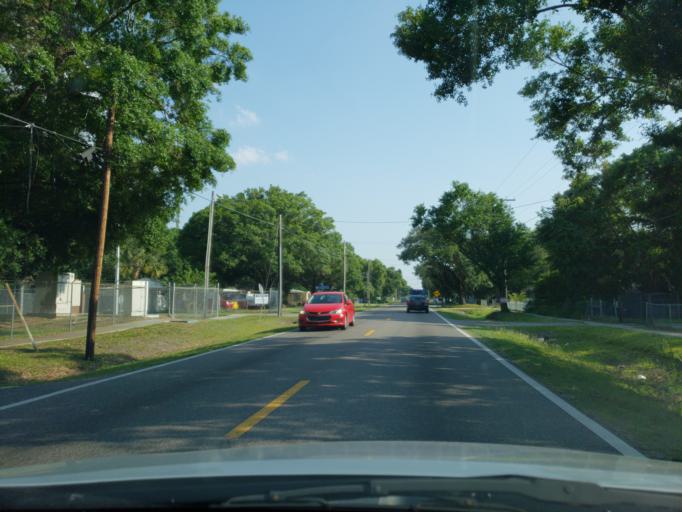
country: US
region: Florida
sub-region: Hillsborough County
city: Palm River-Clair Mel
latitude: 27.9205
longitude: -82.3687
